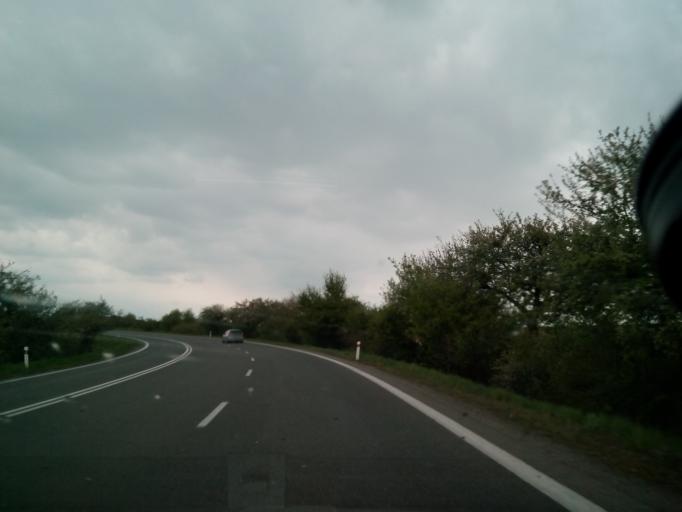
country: SK
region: Kosicky
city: Kosice
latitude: 48.7340
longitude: 21.3941
